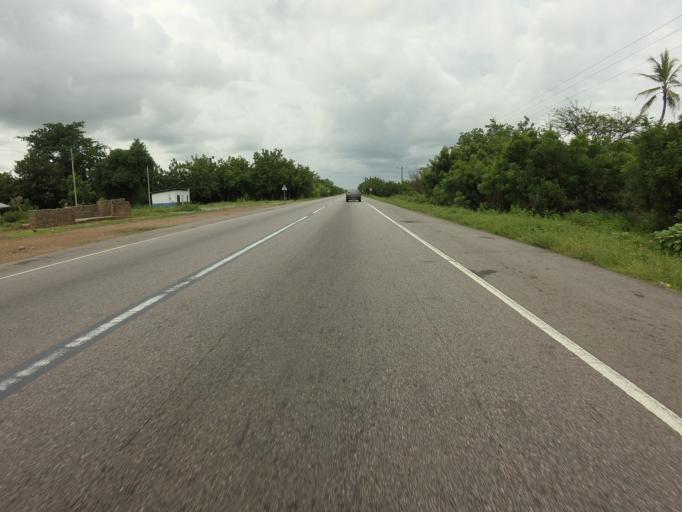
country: GH
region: Northern
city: Tamale
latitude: 8.8911
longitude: -1.4196
